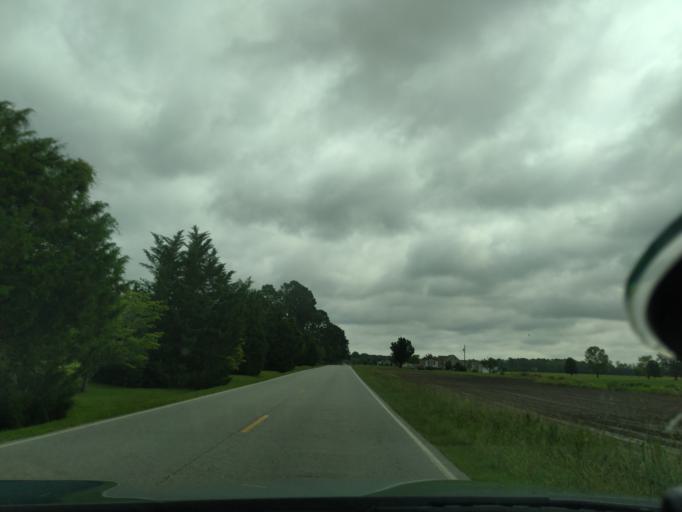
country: US
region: North Carolina
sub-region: Washington County
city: Plymouth
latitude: 35.8639
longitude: -76.7063
